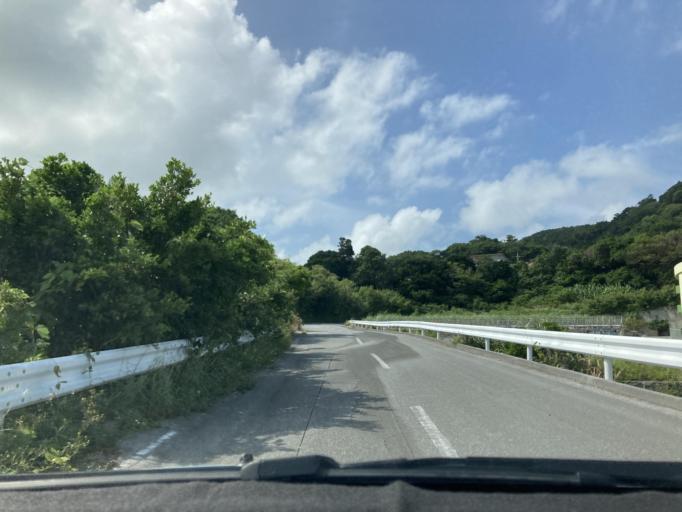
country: JP
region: Okinawa
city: Ginowan
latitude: 26.1527
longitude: 127.8046
